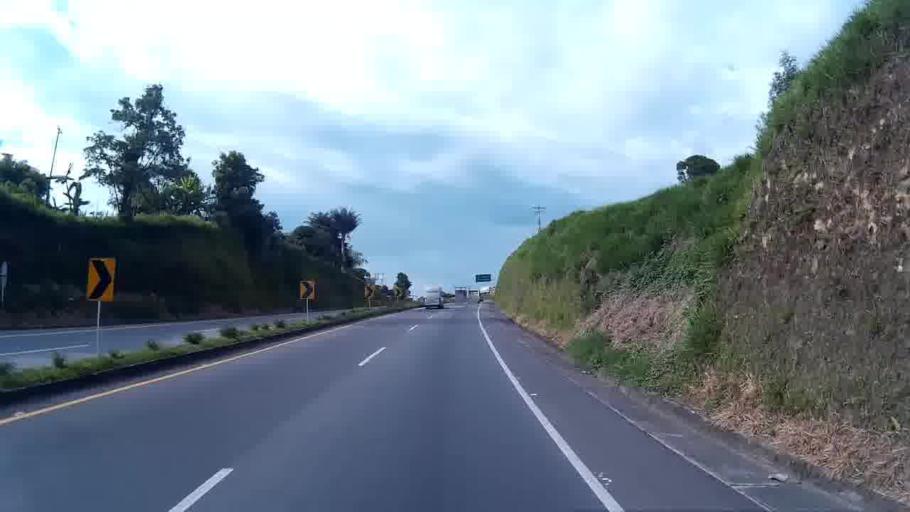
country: CO
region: Quindio
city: Circasia
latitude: 4.6023
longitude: -75.6361
